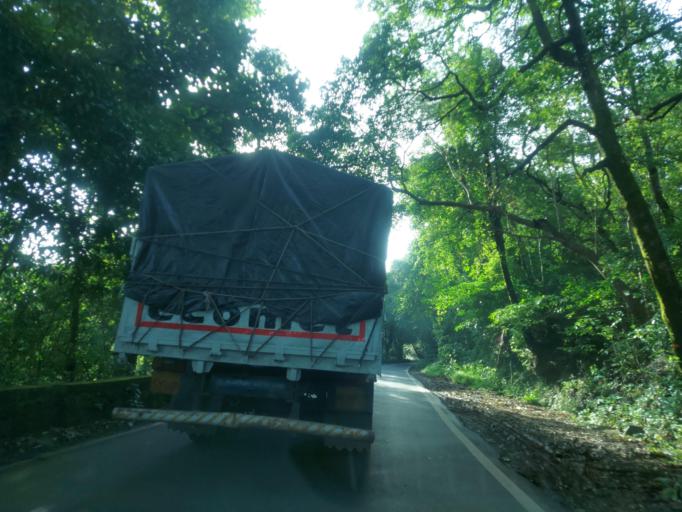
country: IN
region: Maharashtra
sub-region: Sindhudurg
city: Savantvadi
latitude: 15.9357
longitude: 73.9406
